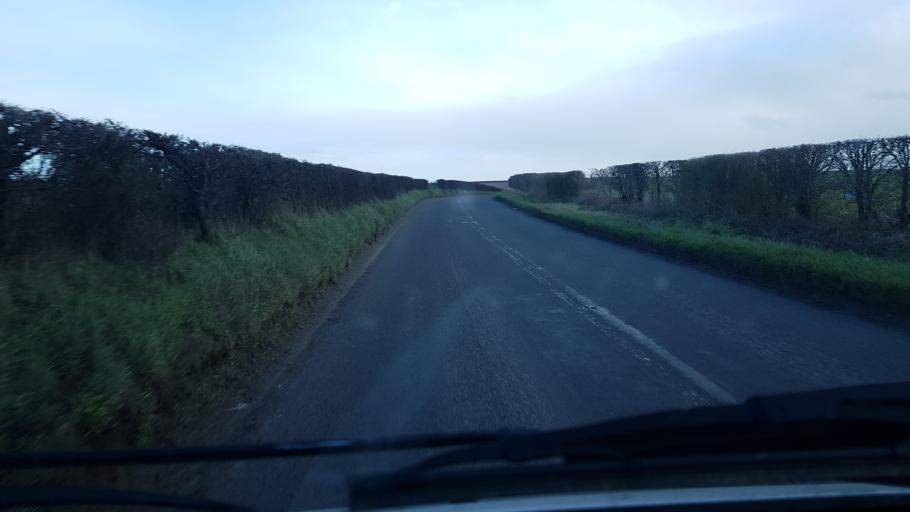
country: GB
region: England
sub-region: Wiltshire
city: Collingbourne Kingston
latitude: 51.2729
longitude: -1.6484
